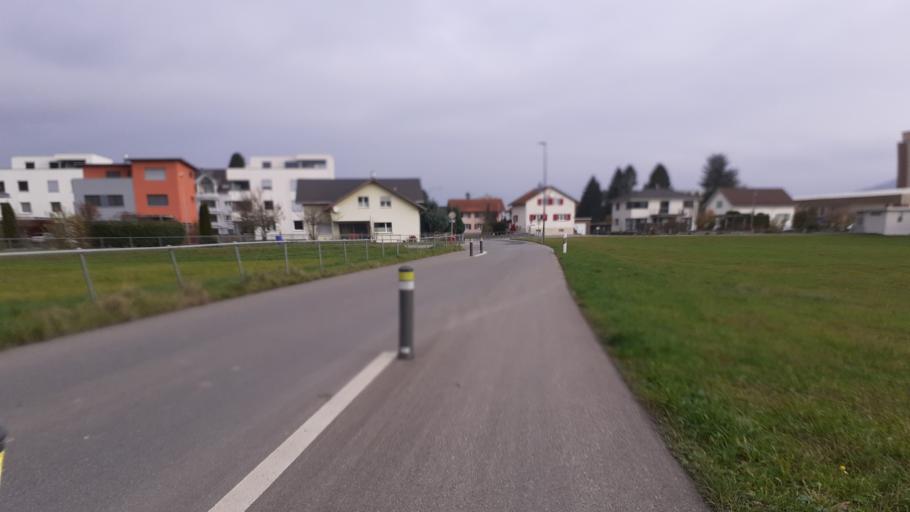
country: CH
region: Saint Gallen
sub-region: Wahlkreis Rheintal
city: Oberriet
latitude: 47.3135
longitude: 9.5664
